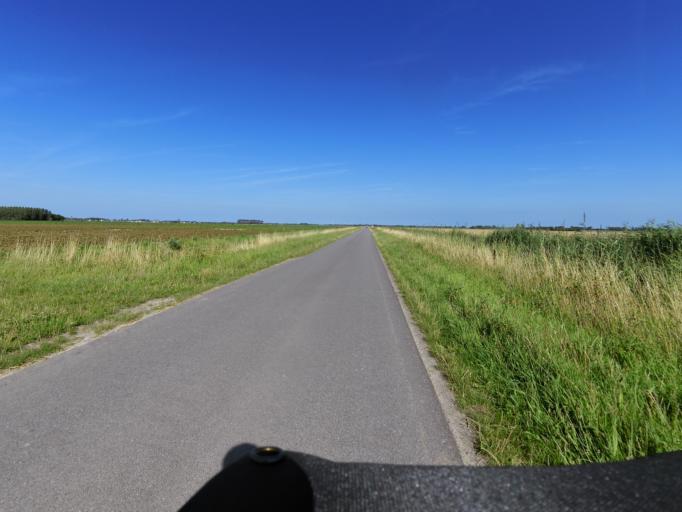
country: NL
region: South Holland
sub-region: Gemeente Goeree-Overflakkee
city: Dirksland
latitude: 51.7290
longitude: 4.0784
